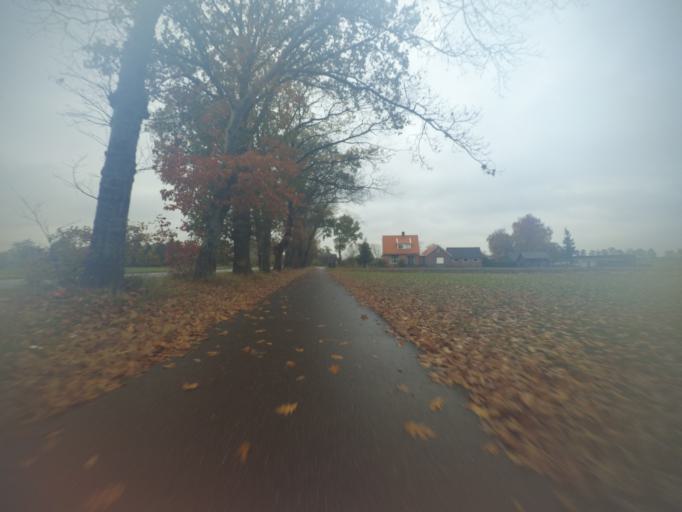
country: NL
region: Gelderland
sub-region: Gemeente Barneveld
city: Barneveld
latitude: 52.1109
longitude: 5.5524
